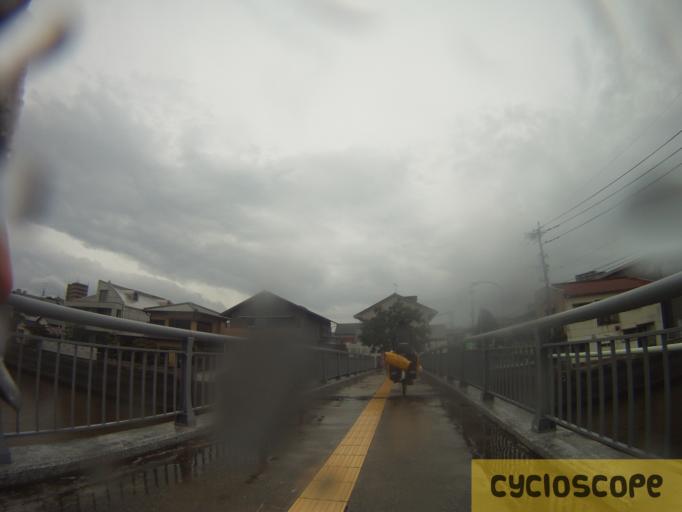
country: JP
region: Fukuoka
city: Fukuoka-shi
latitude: 33.5814
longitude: 130.3432
